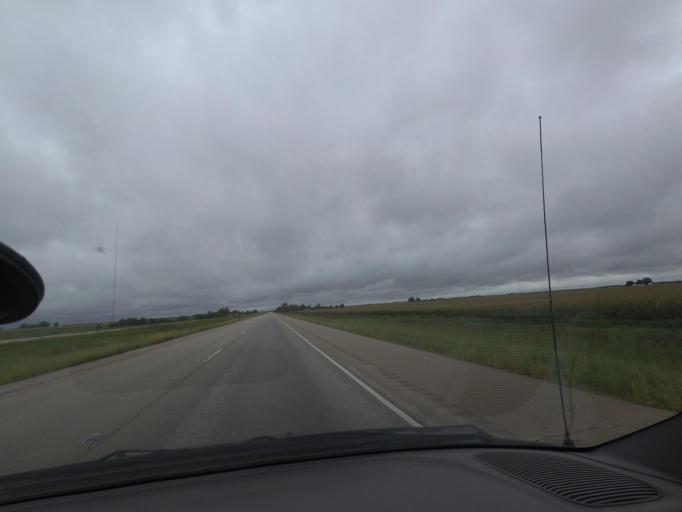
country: US
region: Illinois
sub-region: Macon County
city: Forsyth
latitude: 39.9405
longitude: -88.8345
